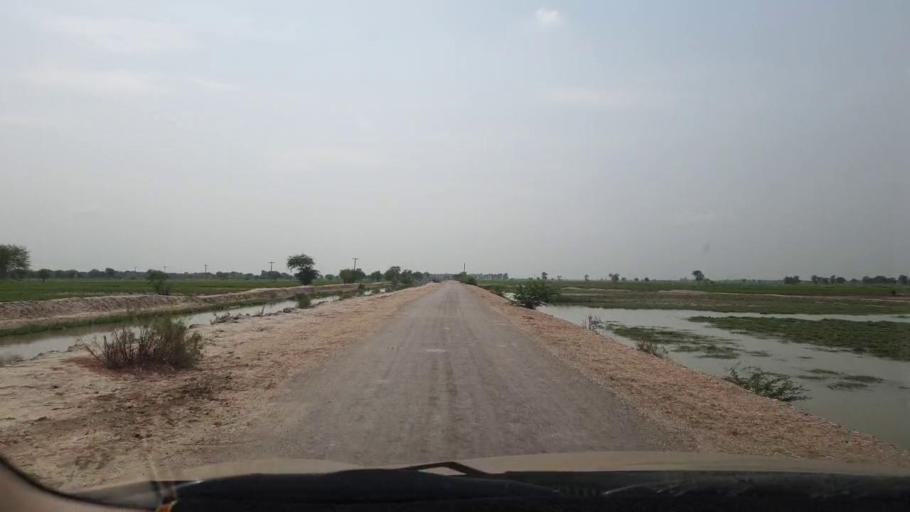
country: PK
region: Sindh
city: Goth Garelo
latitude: 27.5168
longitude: 68.1041
